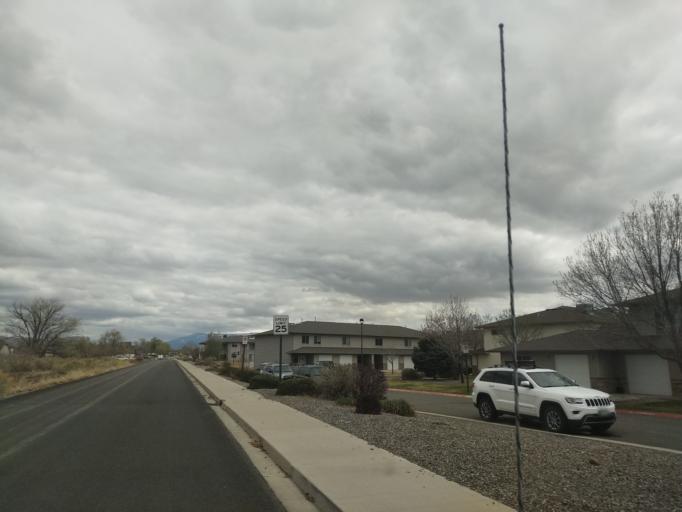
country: US
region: Colorado
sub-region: Mesa County
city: Redlands
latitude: 39.1027
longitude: -108.5966
